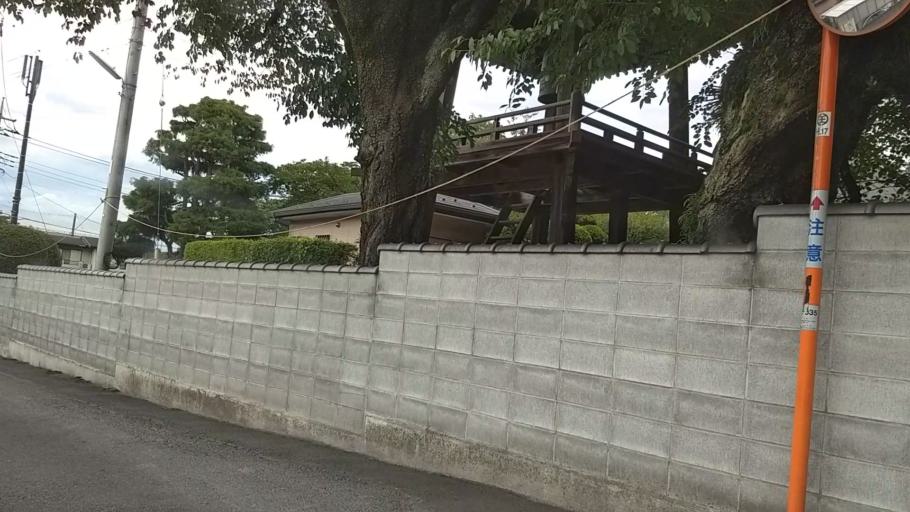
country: JP
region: Tokyo
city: Hachioji
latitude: 35.6478
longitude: 139.3039
